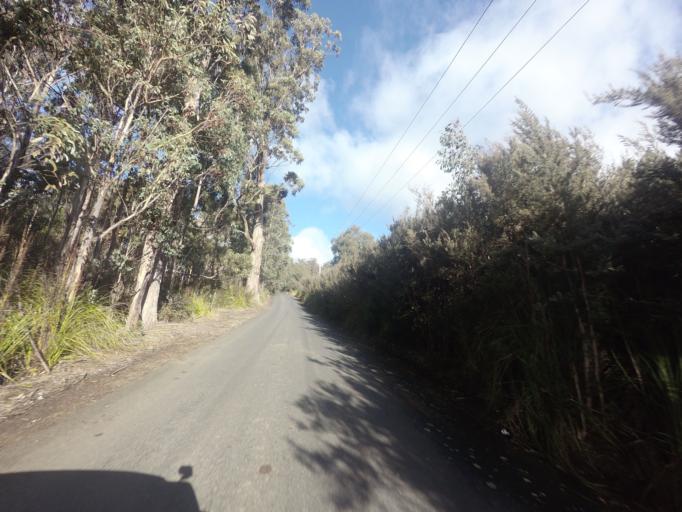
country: AU
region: Tasmania
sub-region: Glenorchy
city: Berriedale
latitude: -42.8392
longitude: 147.1584
